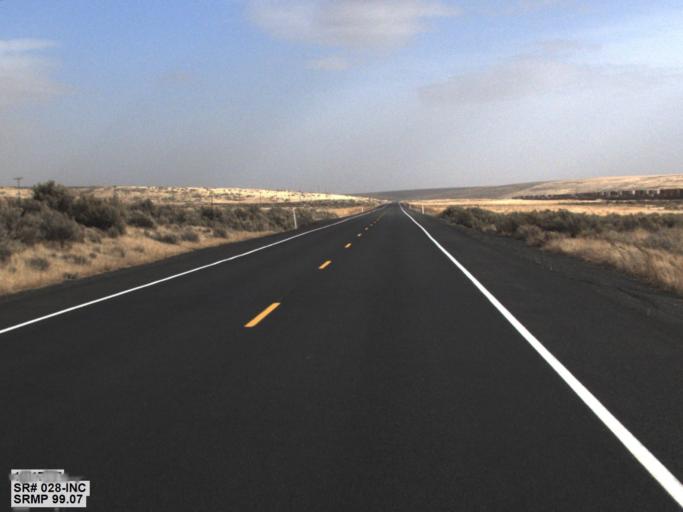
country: US
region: Washington
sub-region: Adams County
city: Ritzville
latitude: 47.3477
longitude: -118.5867
